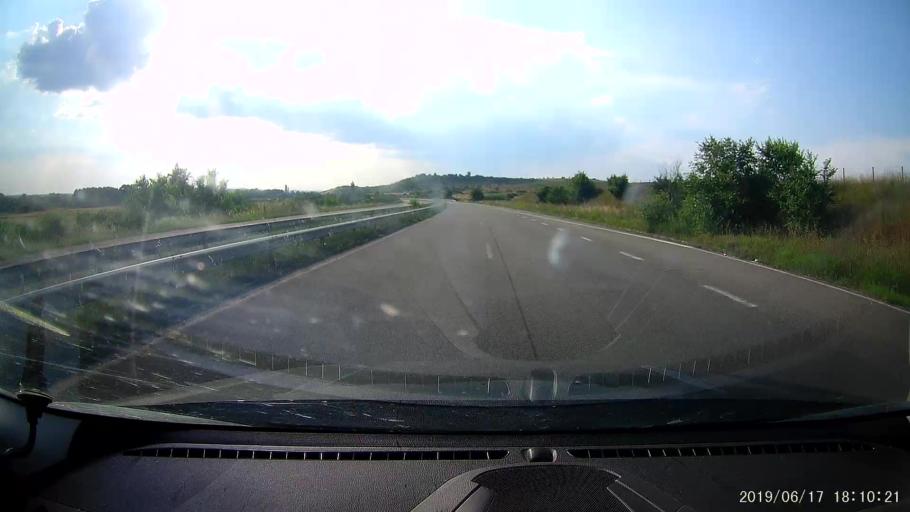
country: BG
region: Khaskovo
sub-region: Obshtina Lyubimets
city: Lyubimets
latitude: 41.8736
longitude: 26.0791
